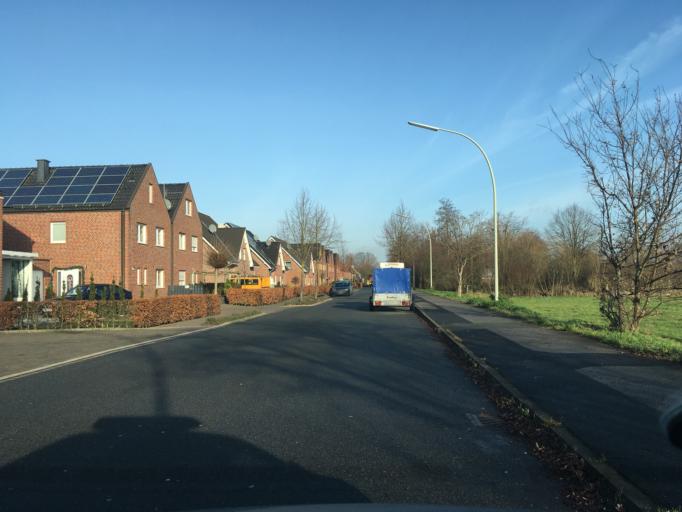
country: DE
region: North Rhine-Westphalia
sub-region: Regierungsbezirk Munster
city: Gescher
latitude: 51.9465
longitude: 6.9886
